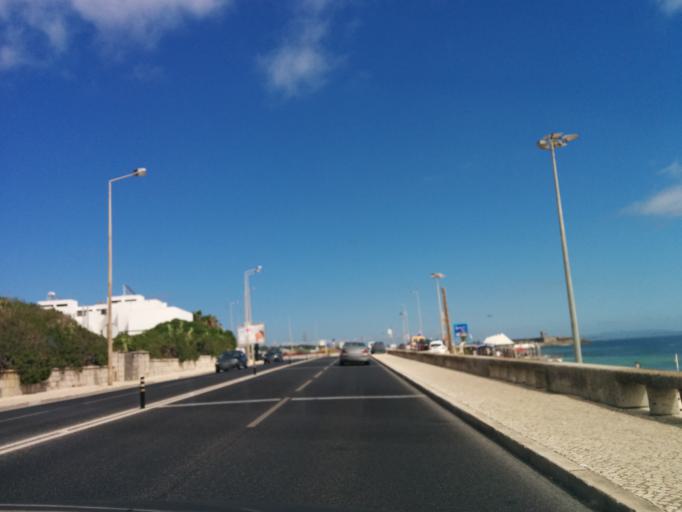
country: PT
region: Lisbon
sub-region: Cascais
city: Parede
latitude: 38.6818
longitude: -9.3409
